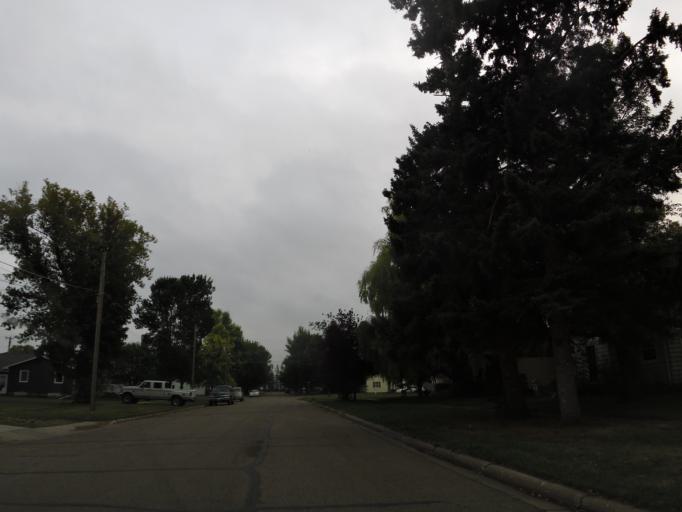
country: US
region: North Dakota
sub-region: Walsh County
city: Grafton
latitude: 48.5589
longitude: -97.1763
